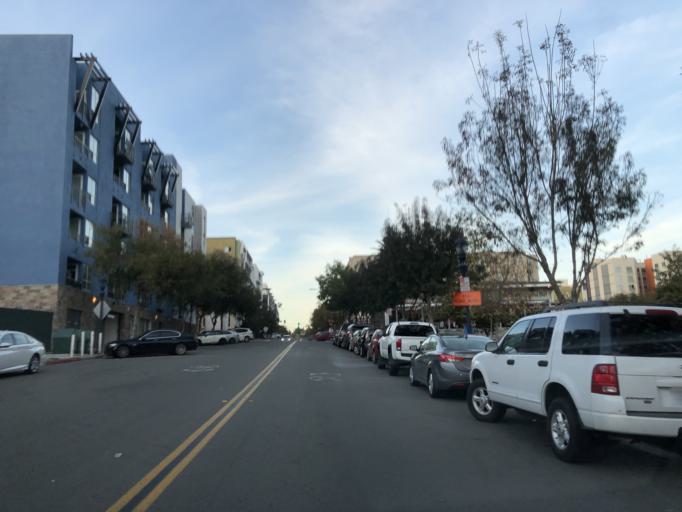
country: US
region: California
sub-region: San Diego County
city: San Diego
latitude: 32.7096
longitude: -117.1519
